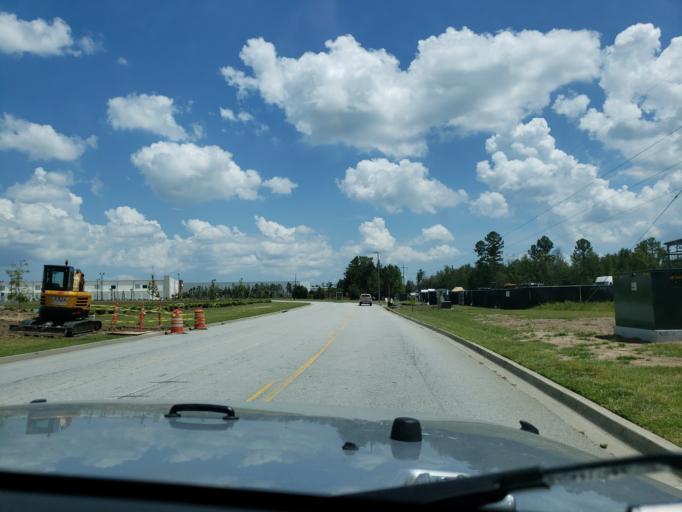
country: US
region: Georgia
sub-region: Chatham County
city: Pooler
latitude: 32.1084
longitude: -81.2778
